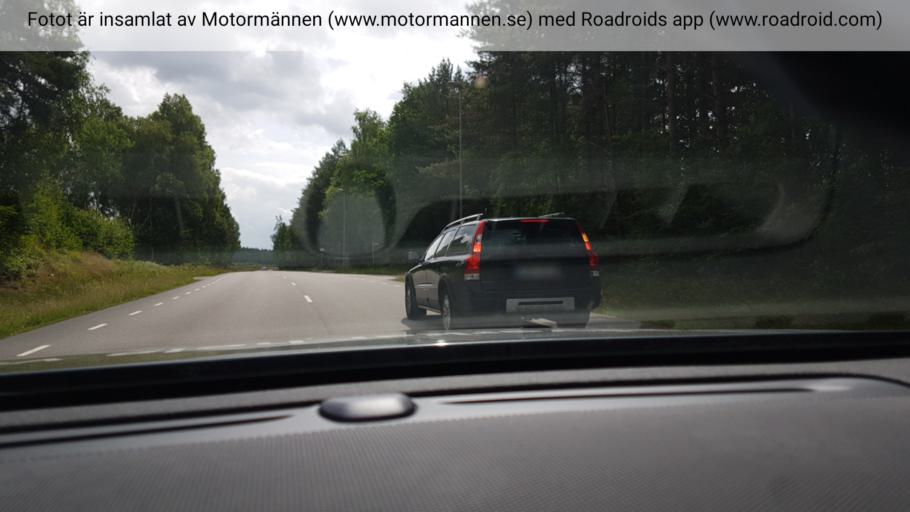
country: SE
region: Skane
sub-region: Hassleholms Kommun
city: Hassleholm
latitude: 56.1761
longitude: 13.7886
